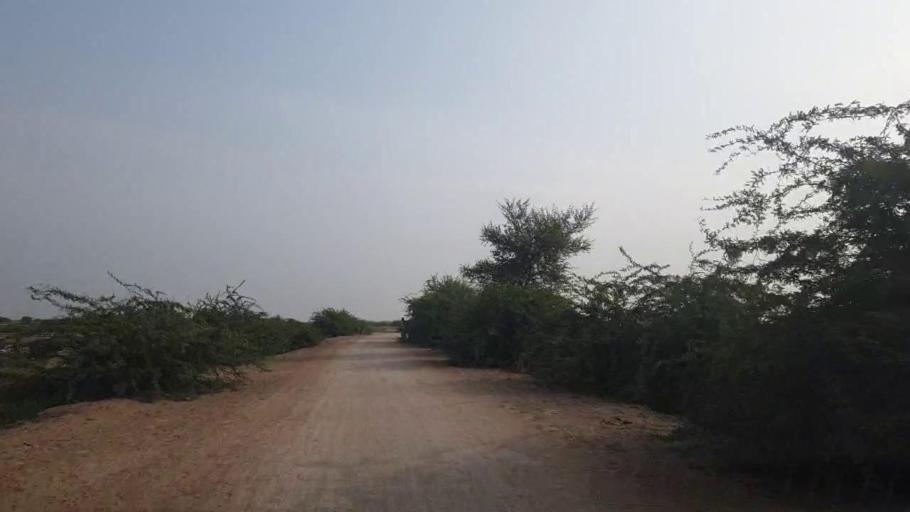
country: PK
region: Sindh
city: Badin
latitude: 24.6077
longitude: 68.6883
